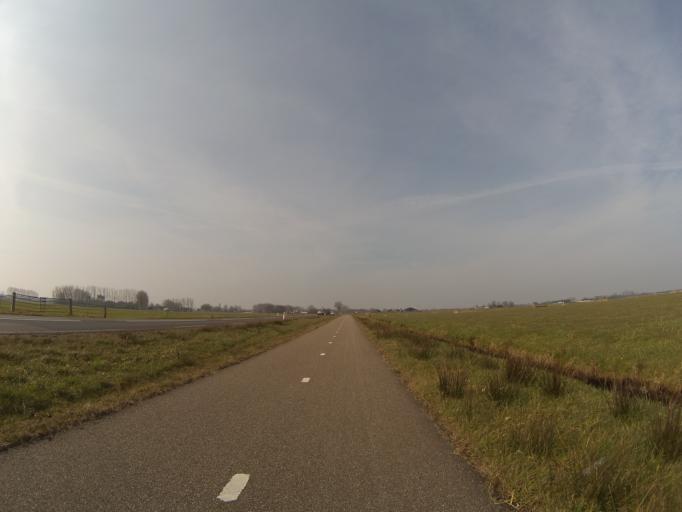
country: NL
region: Utrecht
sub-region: Gemeente Baarn
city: Baarn
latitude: 52.2278
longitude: 5.3241
